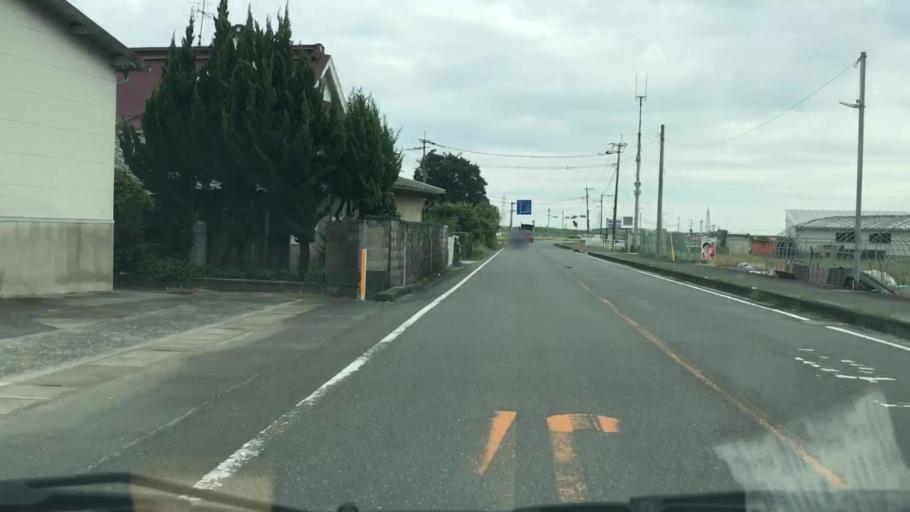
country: JP
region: Saga Prefecture
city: Saga-shi
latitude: 33.2863
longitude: 130.2508
